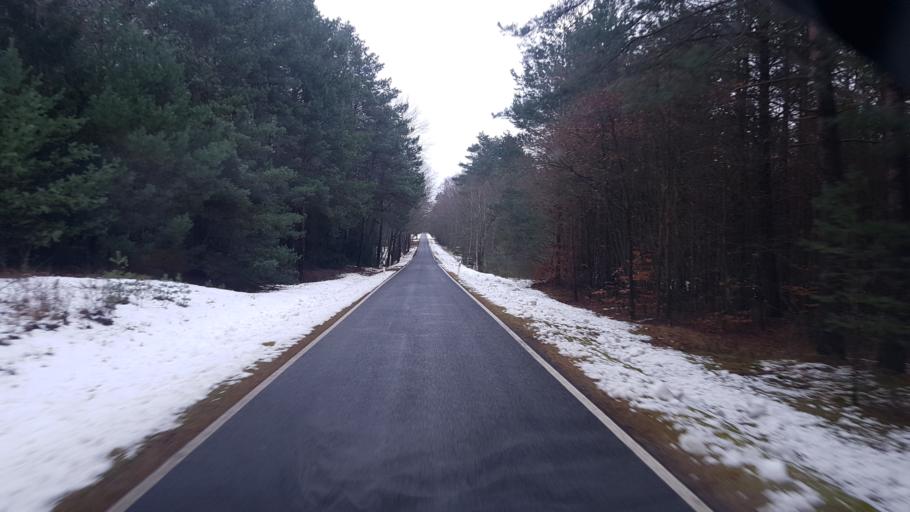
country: DE
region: Brandenburg
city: Jamlitz
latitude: 52.0254
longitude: 14.4524
